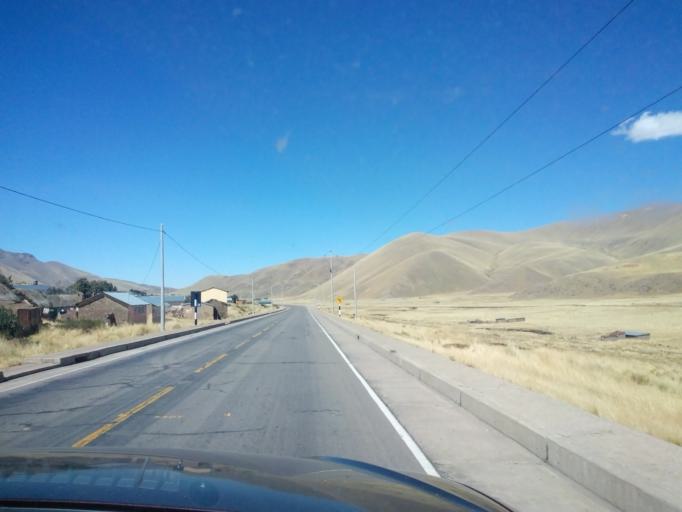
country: PE
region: Puno
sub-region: Provincia de Melgar
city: Santa Rosa
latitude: -14.5112
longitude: -70.9234
